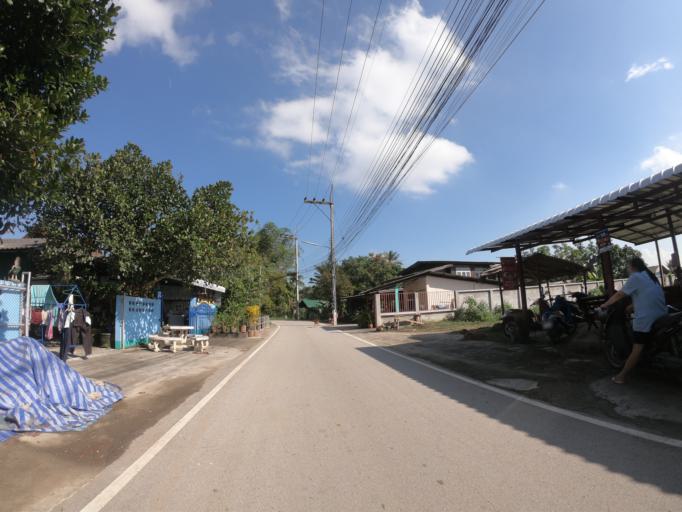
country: TH
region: Chiang Mai
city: Saraphi
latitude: 18.7117
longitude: 99.0189
